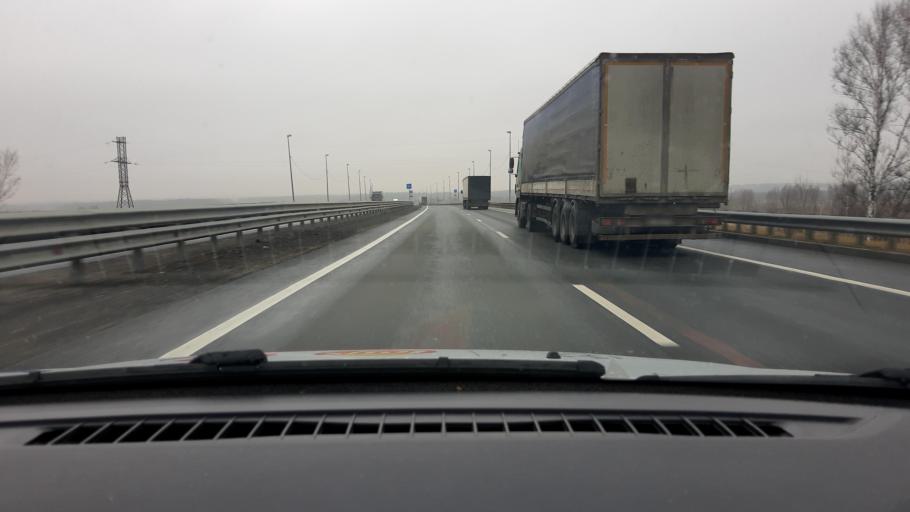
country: RU
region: Nizjnij Novgorod
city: Burevestnik
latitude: 56.1203
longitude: 43.8131
